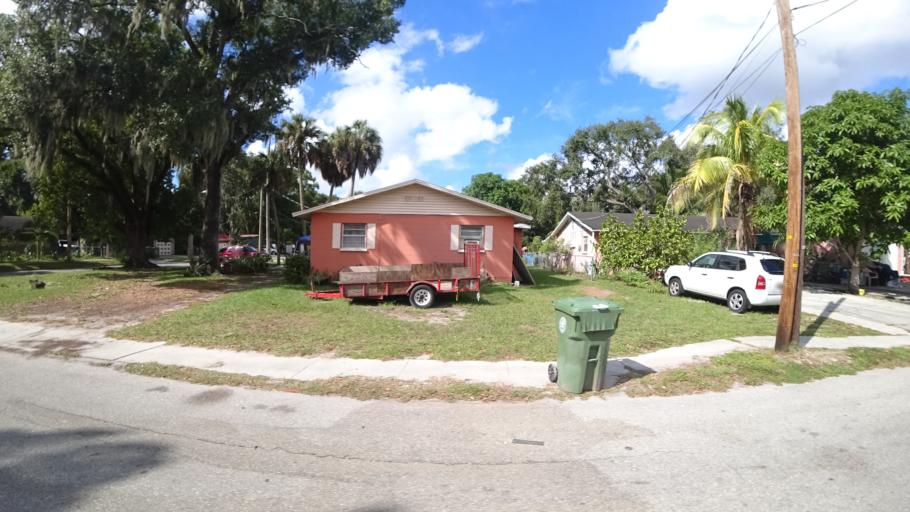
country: US
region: Florida
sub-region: Manatee County
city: Samoset
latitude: 27.4946
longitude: -82.5396
